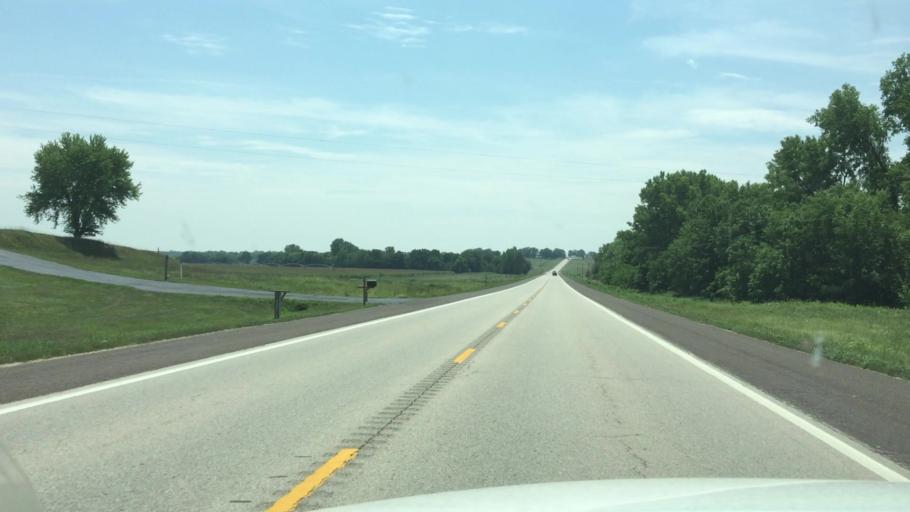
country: US
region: Kansas
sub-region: Jackson County
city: Holton
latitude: 39.5829
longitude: -95.7322
